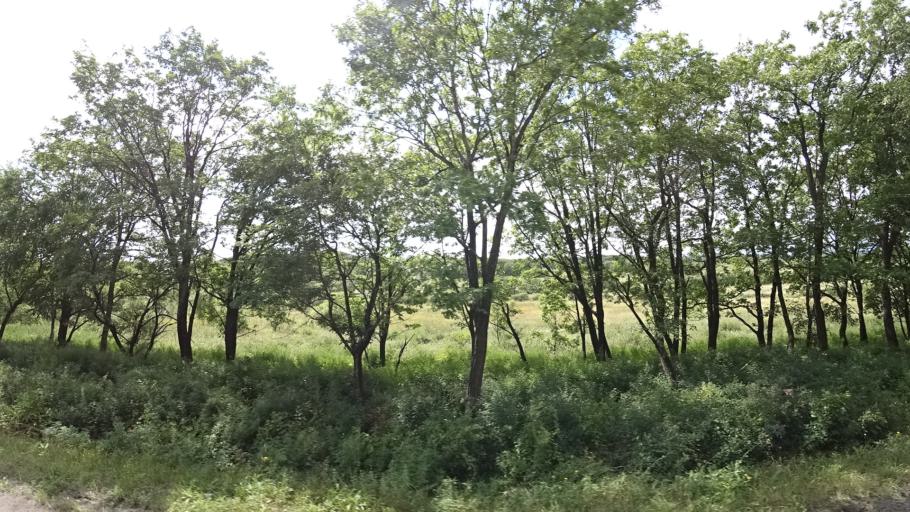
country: RU
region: Primorskiy
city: Lyalichi
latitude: 44.1506
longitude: 132.3928
